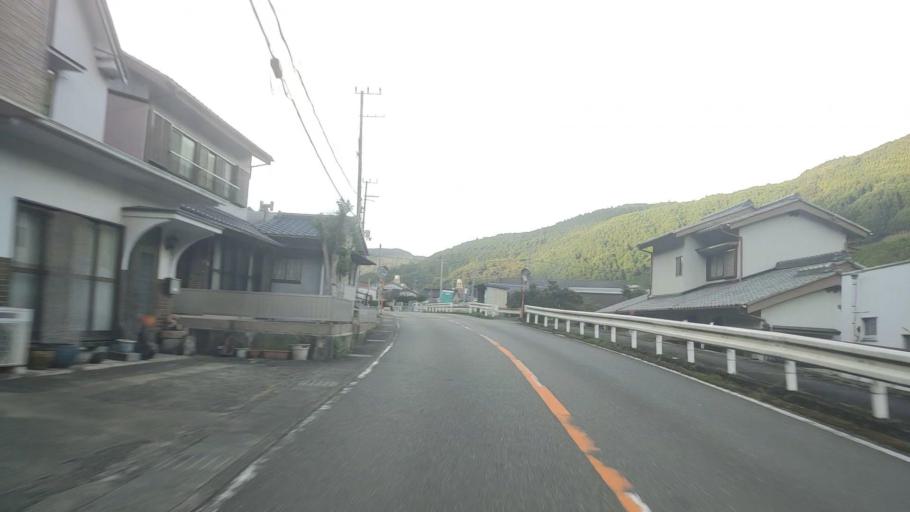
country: JP
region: Wakayama
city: Tanabe
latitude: 33.7903
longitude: 135.5157
